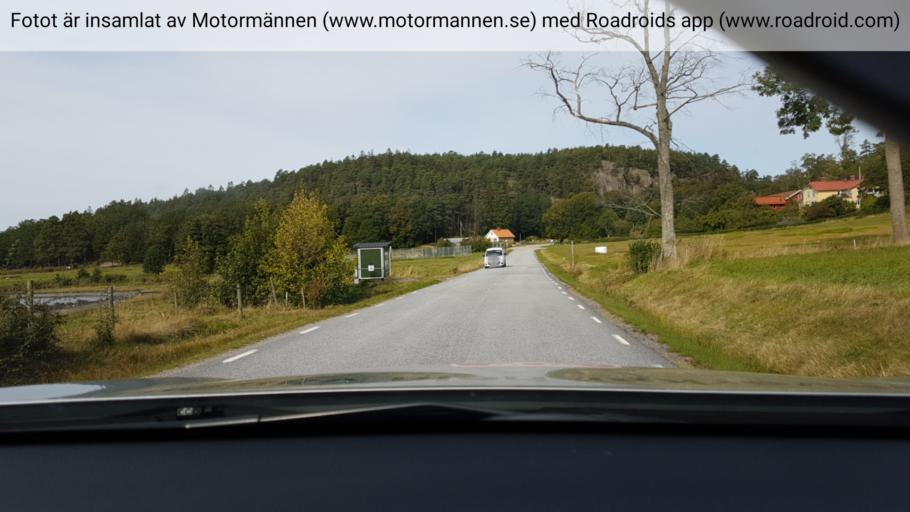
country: SE
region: Vaestra Goetaland
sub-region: Uddevalla Kommun
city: Ljungskile
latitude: 58.2585
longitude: 11.8536
